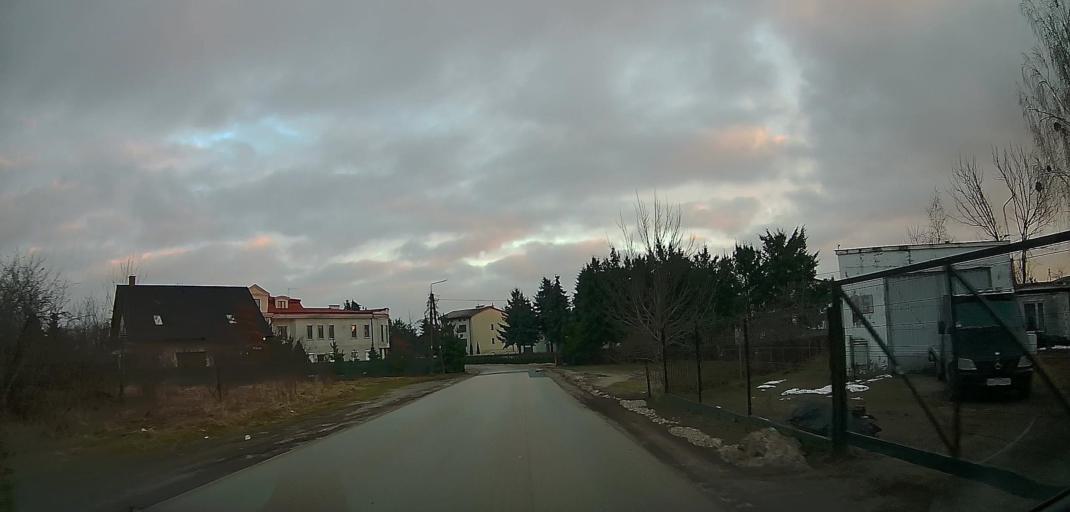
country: PL
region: Masovian Voivodeship
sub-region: Radom
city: Radom
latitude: 51.4479
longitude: 21.1402
